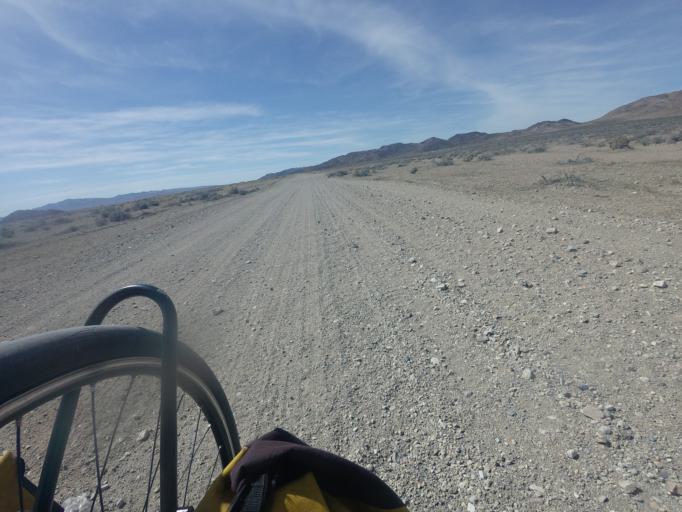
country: US
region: California
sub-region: San Bernardino County
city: Searles Valley
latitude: 35.5944
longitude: -117.4086
